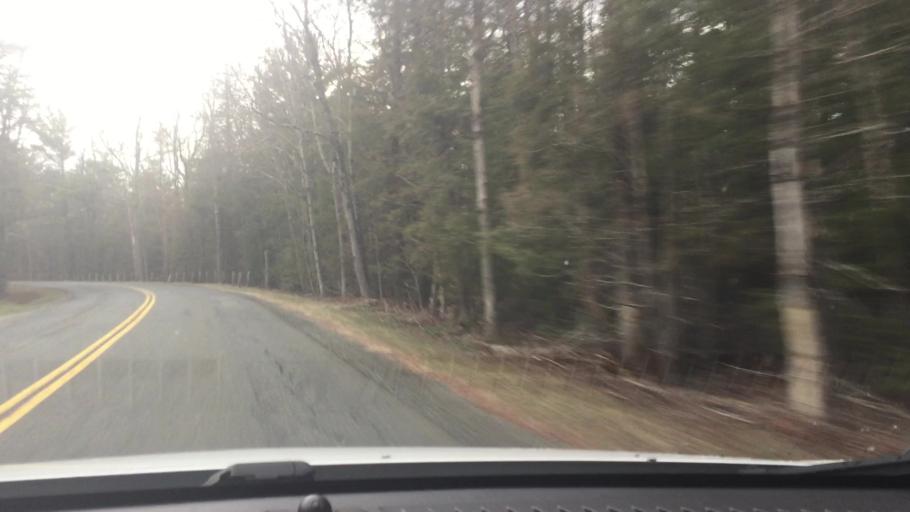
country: US
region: Massachusetts
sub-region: Berkshire County
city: Otis
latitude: 42.1830
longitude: -73.0283
